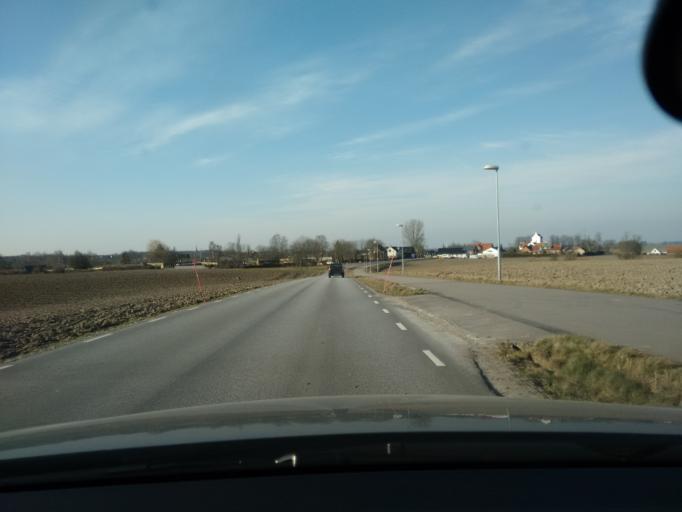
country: SE
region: Skane
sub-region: Lunds Kommun
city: Lund
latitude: 55.7425
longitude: 13.1785
